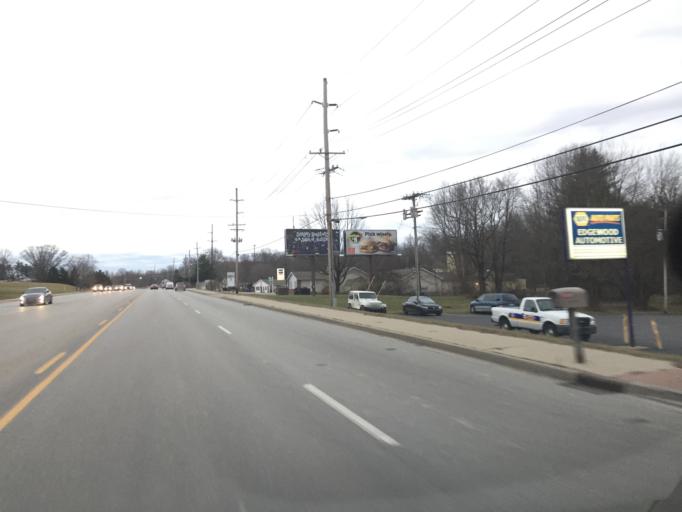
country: US
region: Indiana
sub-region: Monroe County
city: Ellettsville
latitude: 39.2194
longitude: -86.6029
